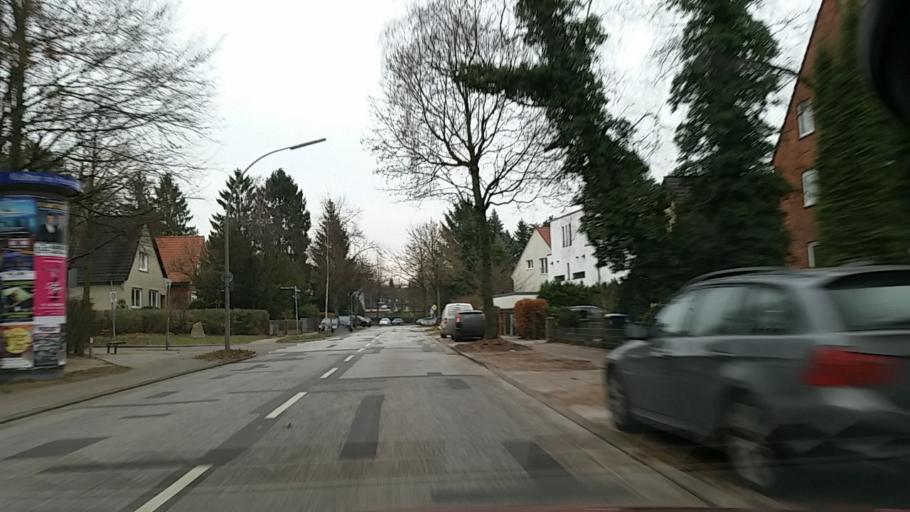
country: DE
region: Hamburg
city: Stellingen
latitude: 53.6296
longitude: 9.9410
